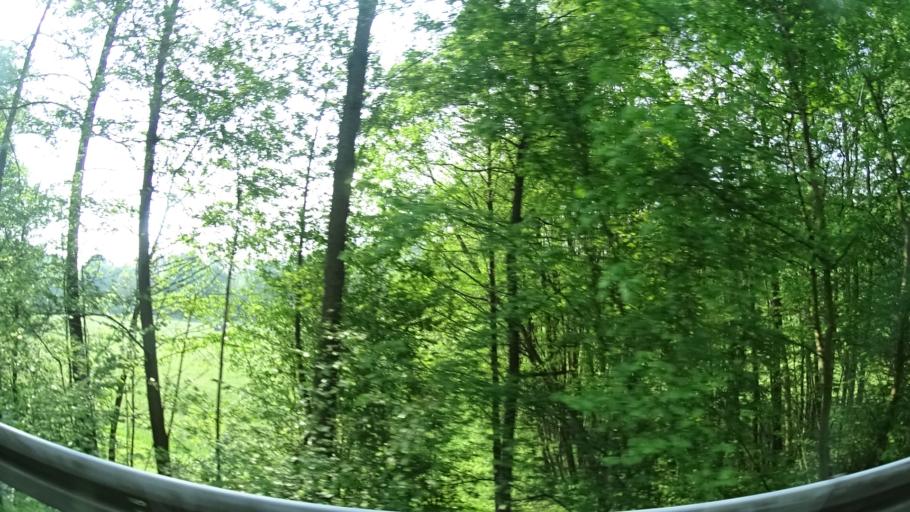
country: DE
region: Bavaria
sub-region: Regierungsbezirk Unterfranken
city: Heimbuchenthal
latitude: 49.8605
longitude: 9.2966
